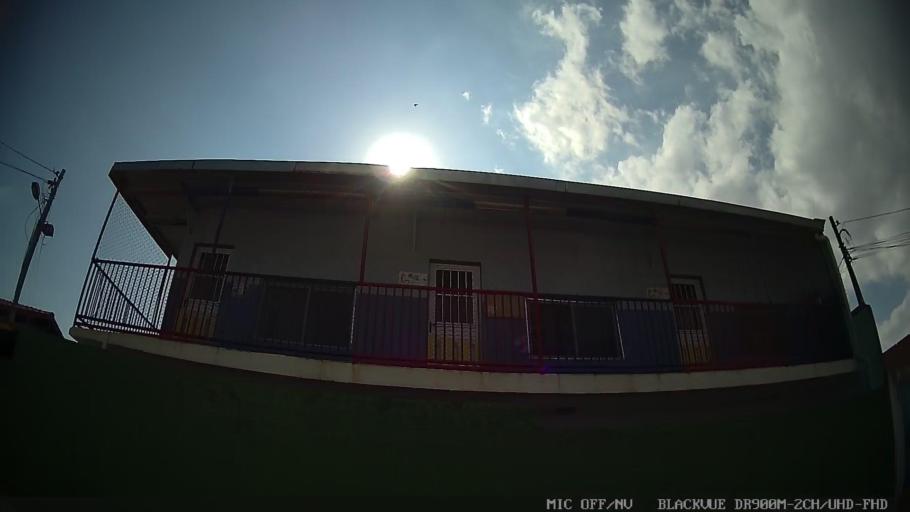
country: BR
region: Sao Paulo
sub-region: Ferraz De Vasconcelos
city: Ferraz de Vasconcelos
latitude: -23.4999
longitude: -46.4480
